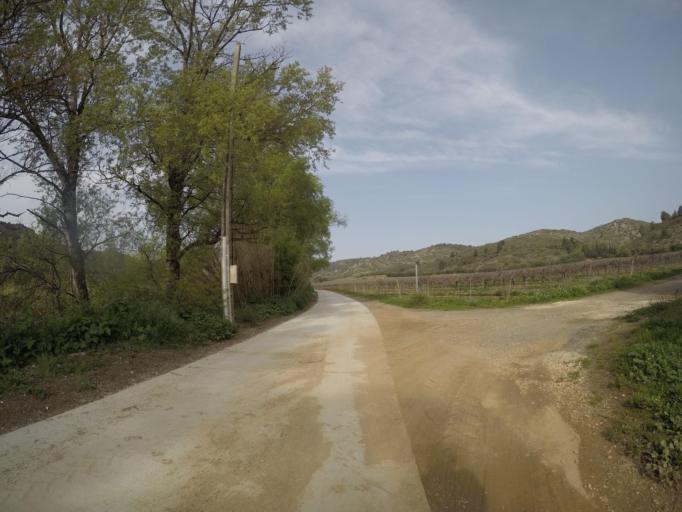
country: FR
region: Languedoc-Roussillon
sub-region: Departement des Pyrenees-Orientales
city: Estagel
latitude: 42.7770
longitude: 2.7383
